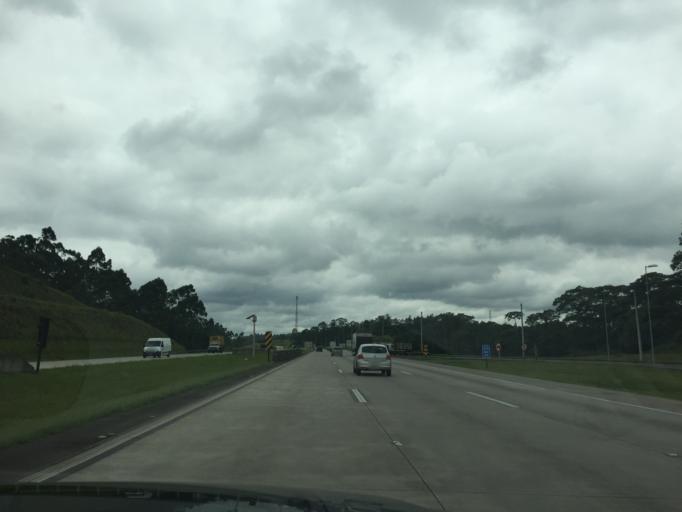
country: BR
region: Sao Paulo
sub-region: Diadema
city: Diadema
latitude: -23.7911
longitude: -46.6484
